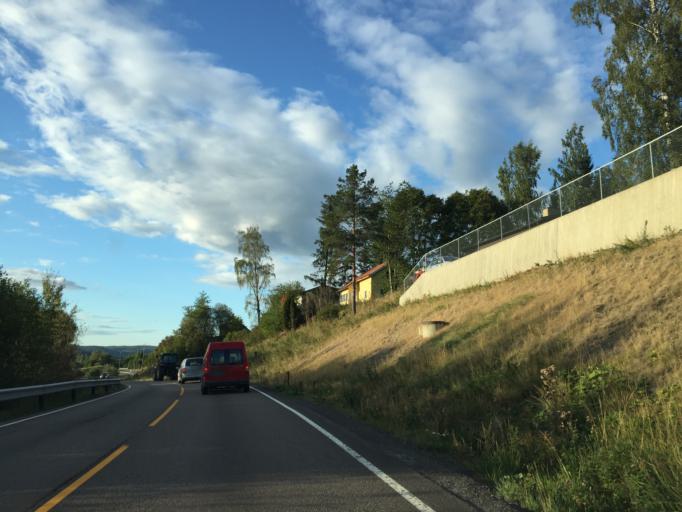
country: NO
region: Akershus
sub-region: Fet
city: Fetsund
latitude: 59.9155
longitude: 11.1844
